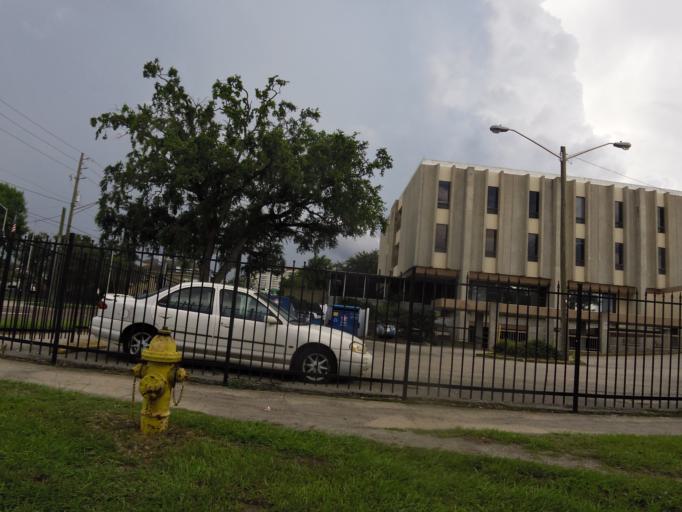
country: US
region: Florida
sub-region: Duval County
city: Jacksonville
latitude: 30.3303
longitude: -81.6514
